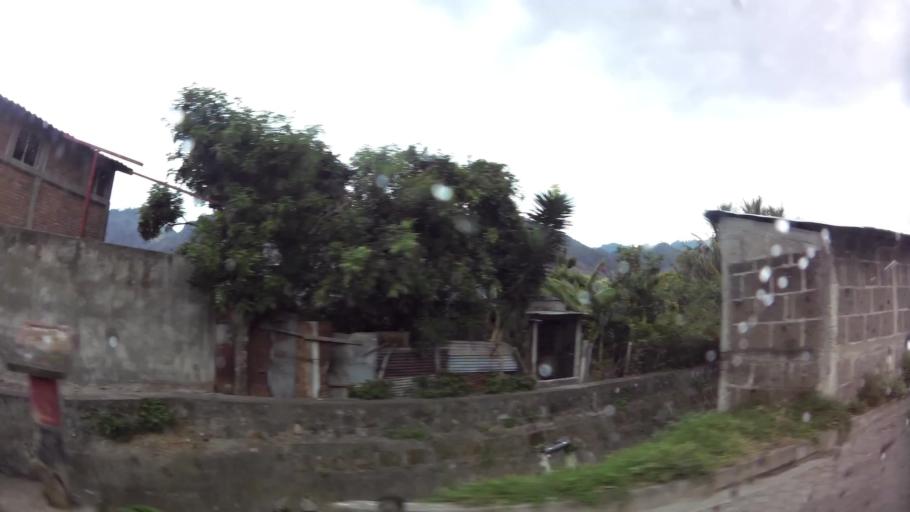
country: NI
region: Jinotega
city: Jinotega
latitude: 13.0975
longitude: -86.0009
